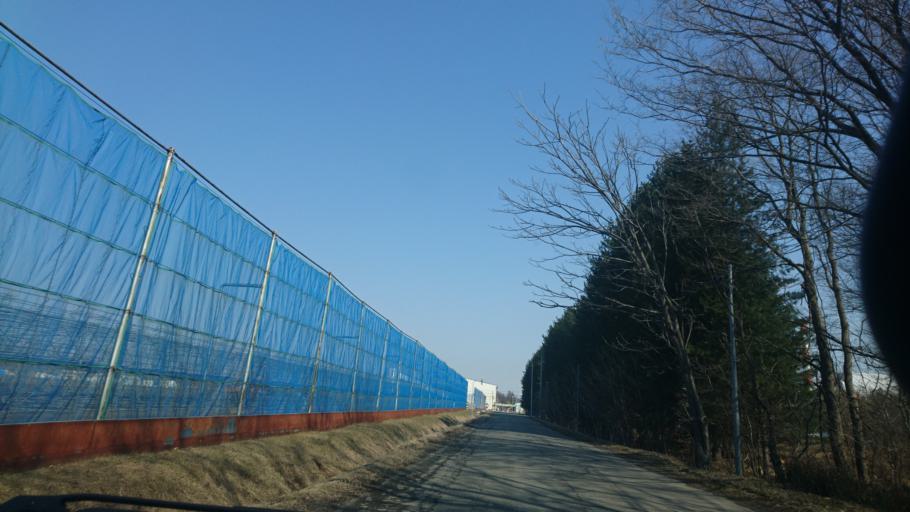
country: JP
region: Hokkaido
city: Obihiro
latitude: 42.9181
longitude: 143.0762
